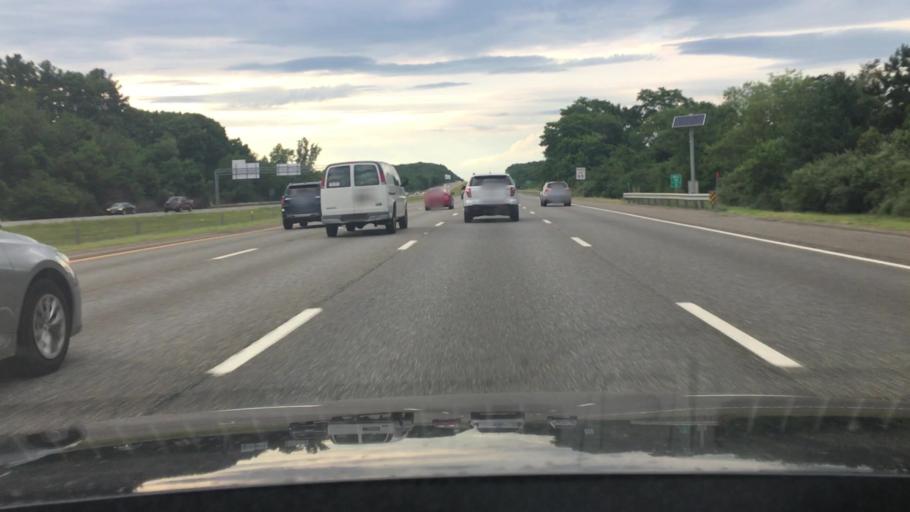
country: US
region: Massachusetts
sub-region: Essex County
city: Danvers
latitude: 42.5980
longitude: -70.9646
